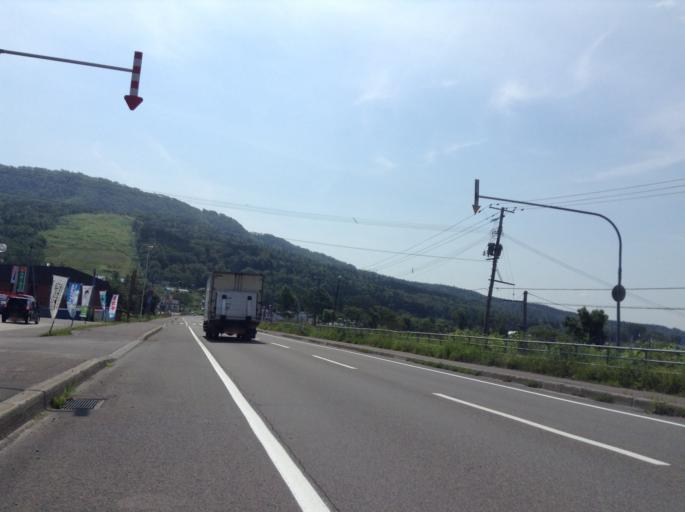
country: JP
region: Hokkaido
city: Nayoro
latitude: 44.7247
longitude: 142.2648
